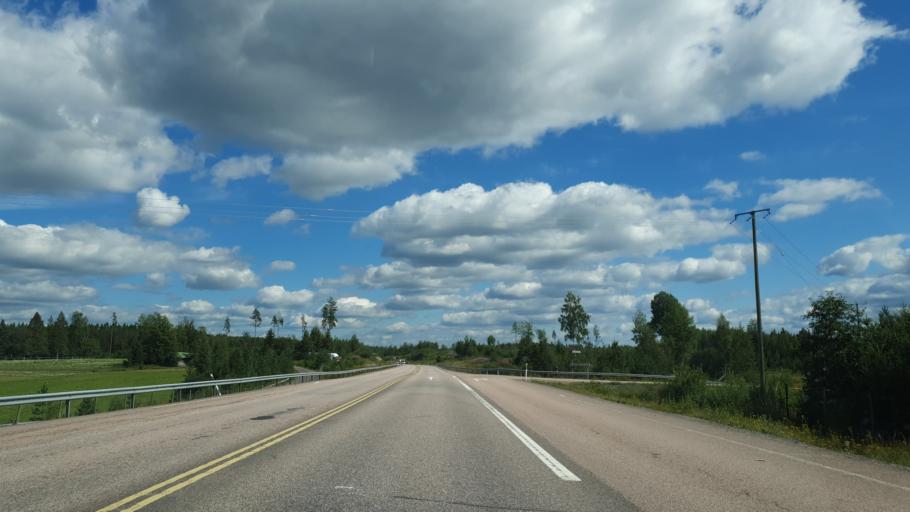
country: FI
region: Pirkanmaa
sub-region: Tampere
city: Kuhmalahti
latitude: 61.7075
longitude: 24.5806
